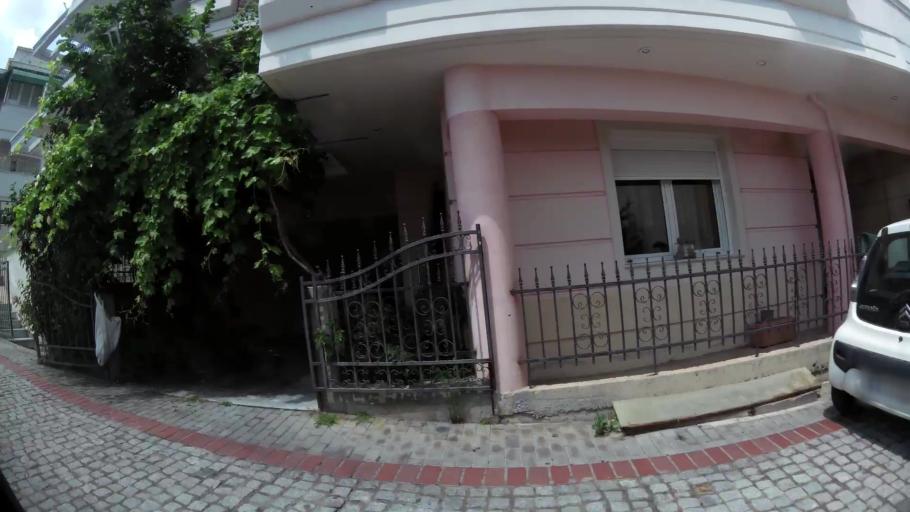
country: GR
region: West Macedonia
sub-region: Nomos Kozanis
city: Kozani
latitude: 40.3048
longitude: 21.7917
